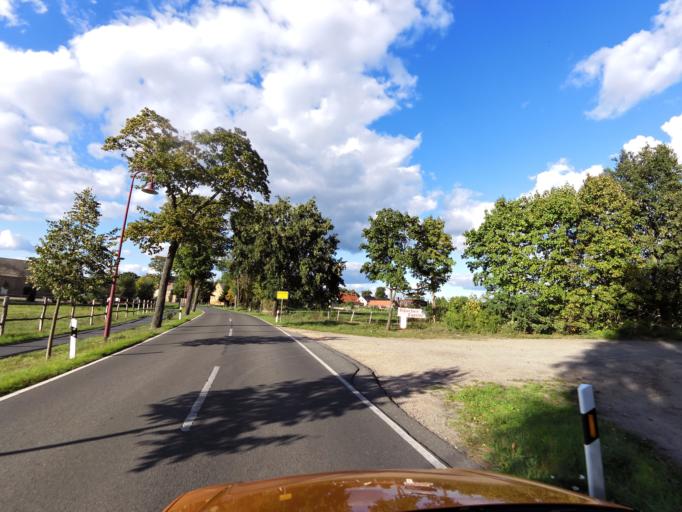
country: DE
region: Brandenburg
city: Trebbin
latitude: 52.1596
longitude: 13.1847
